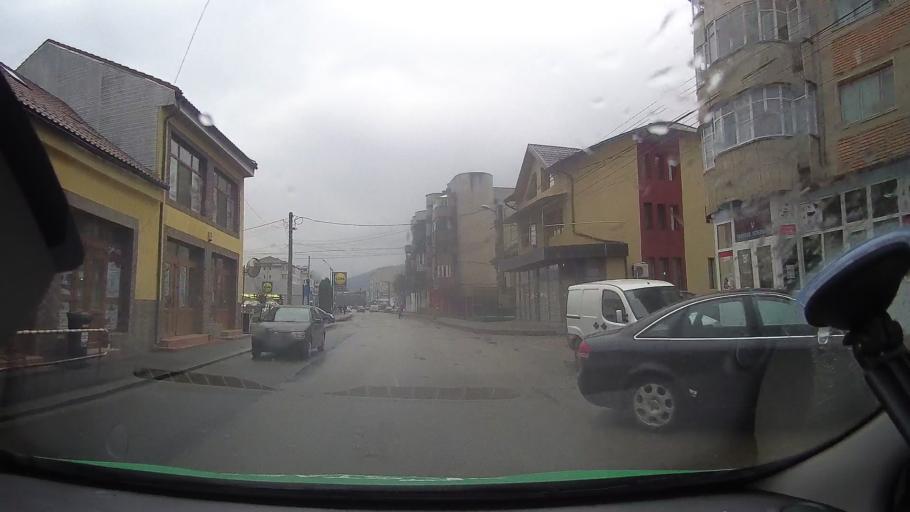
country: RO
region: Hunedoara
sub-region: Municipiul Brad
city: Brad
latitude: 46.1324
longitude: 22.7881
